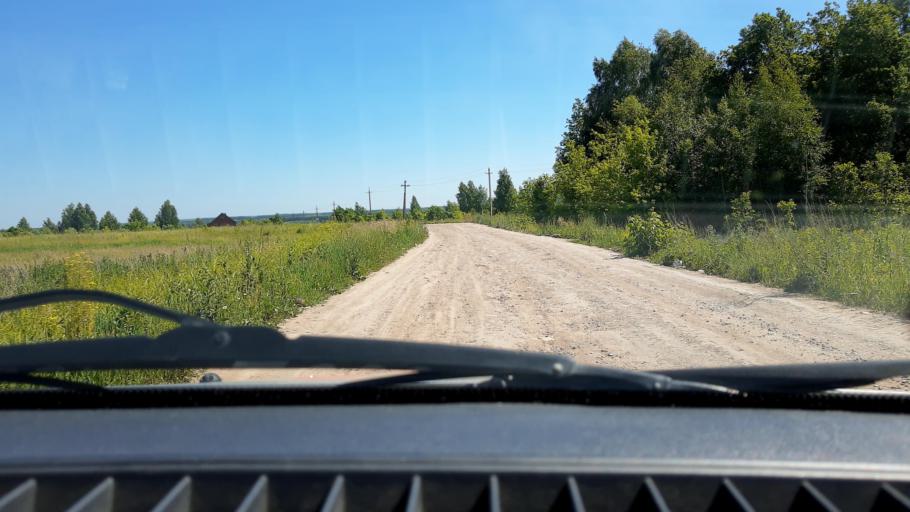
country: RU
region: Bashkortostan
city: Avdon
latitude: 54.5536
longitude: 55.7052
